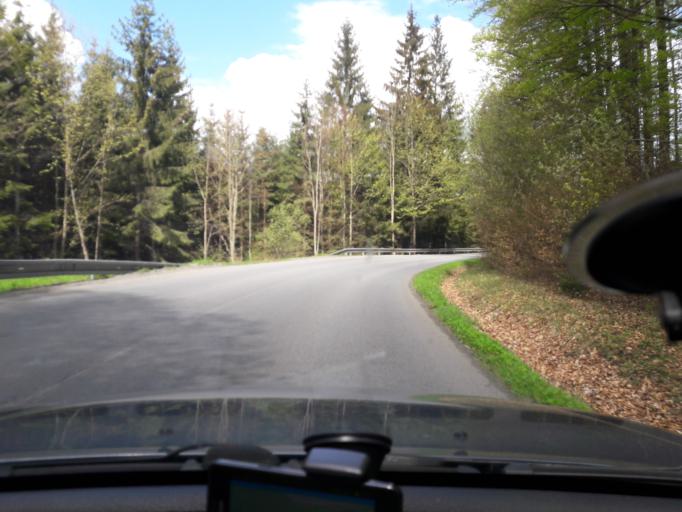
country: SK
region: Banskobystricky
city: Hrinova
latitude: 48.6364
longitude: 19.5792
